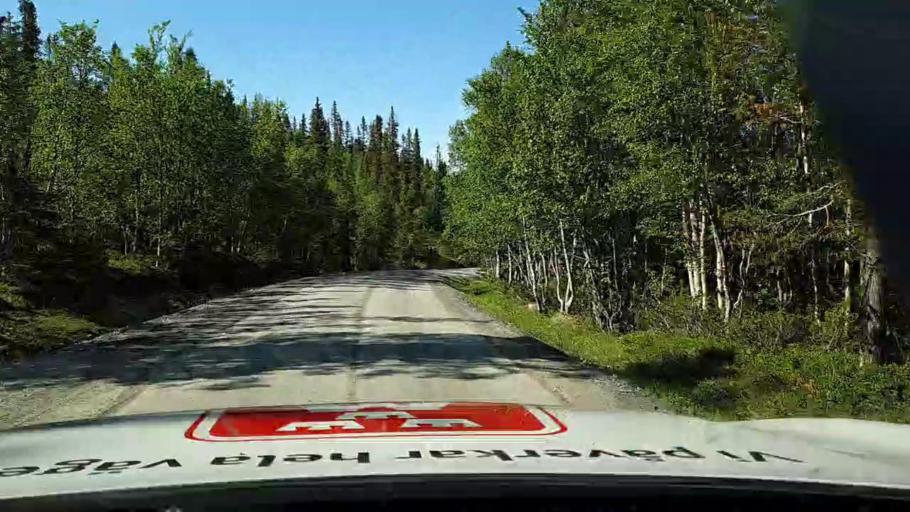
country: SE
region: Jaemtland
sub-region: Are Kommun
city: Are
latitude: 62.7948
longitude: 12.7616
